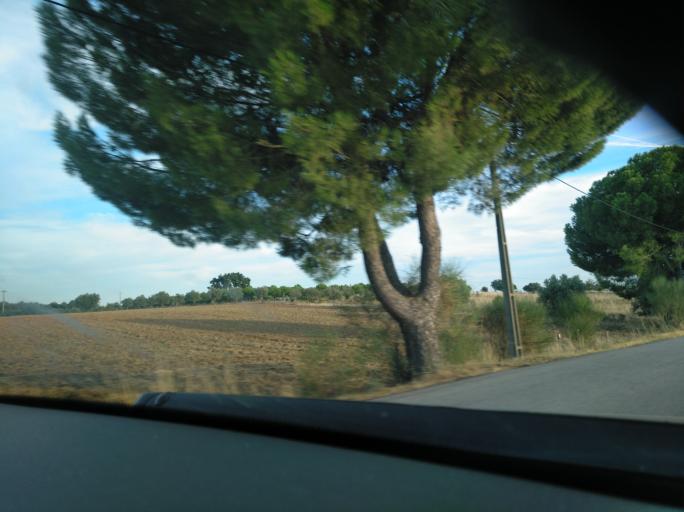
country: PT
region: Evora
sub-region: Arraiolos
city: Arraiolos
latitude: 38.8464
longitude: -7.8289
